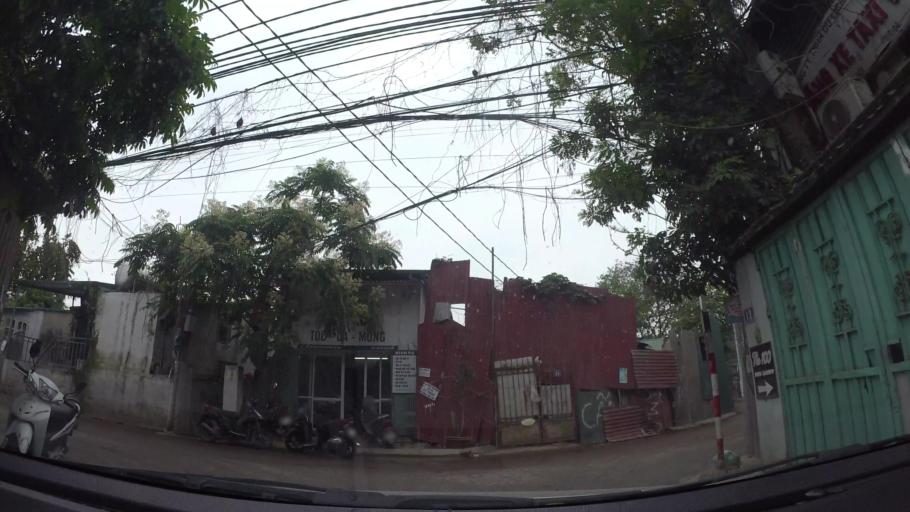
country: VN
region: Ha Noi
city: Tay Ho
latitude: 21.0694
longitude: 105.8296
